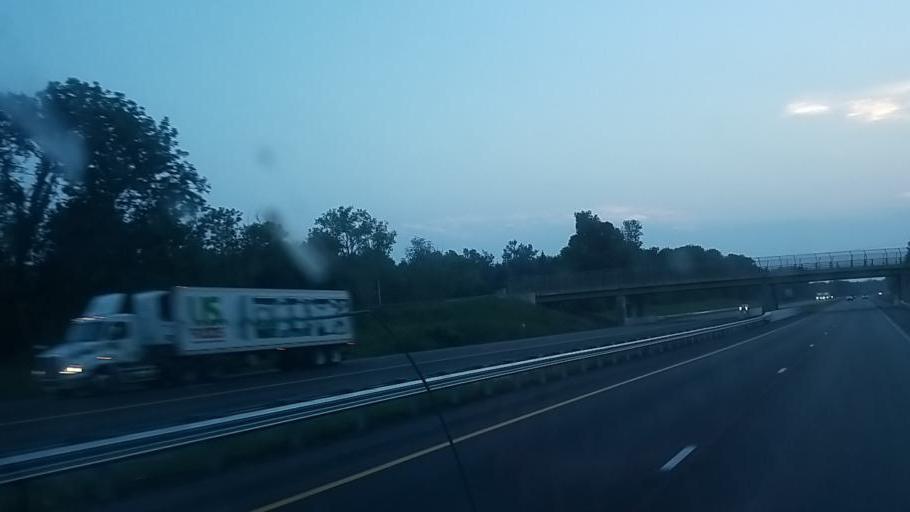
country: US
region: New York
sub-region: Oneida County
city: Clark Mills
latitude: 43.1280
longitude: -75.4365
